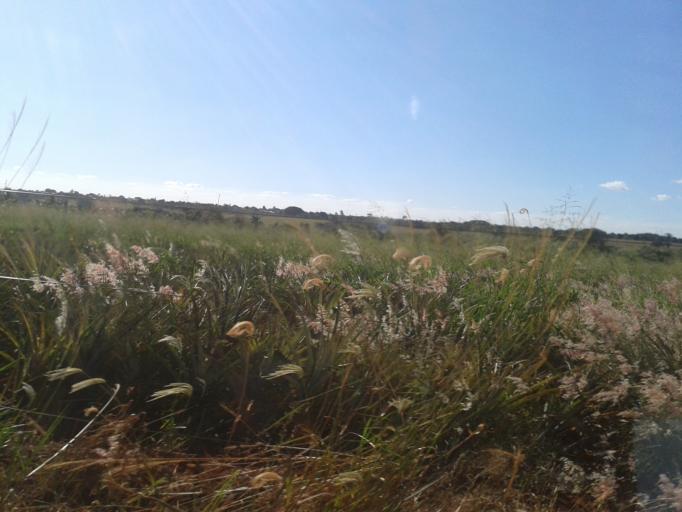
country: BR
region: Minas Gerais
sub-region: Centralina
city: Centralina
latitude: -18.7404
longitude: -49.1878
